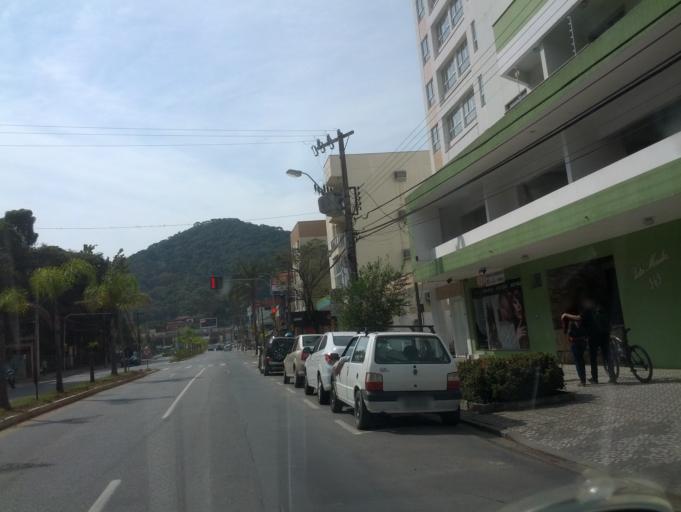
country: BR
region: Santa Catarina
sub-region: Blumenau
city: Blumenau
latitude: -26.9074
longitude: -49.0793
